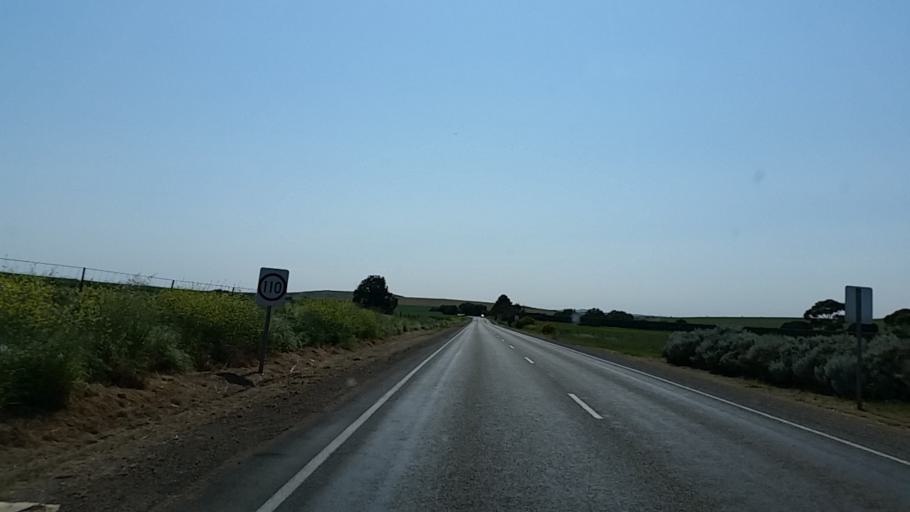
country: AU
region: South Australia
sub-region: Port Pirie City and Dists
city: Crystal Brook
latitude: -33.2549
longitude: 138.3610
